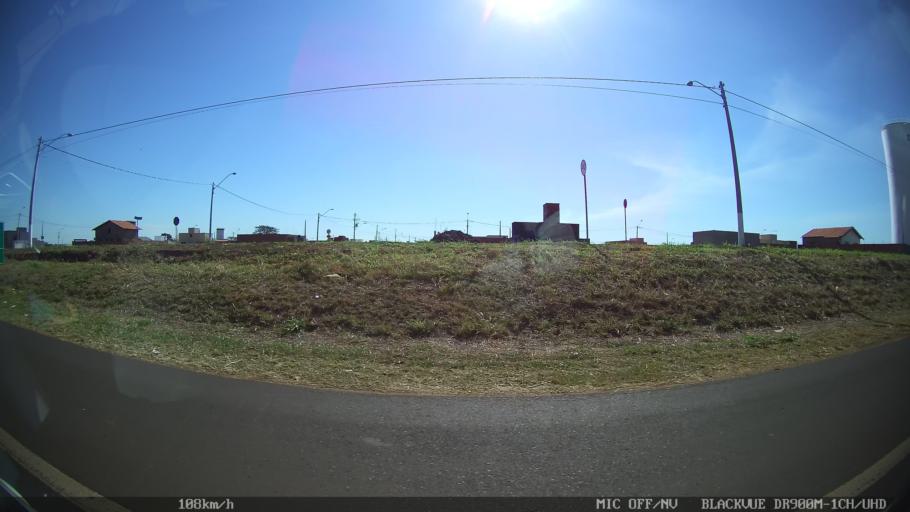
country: BR
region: Sao Paulo
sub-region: Olimpia
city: Olimpia
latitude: -20.7314
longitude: -48.8708
